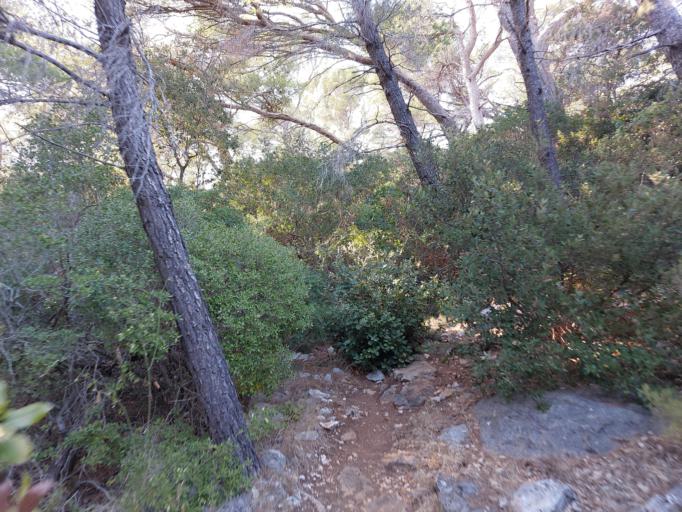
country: HR
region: Dubrovacko-Neretvanska
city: Smokvica
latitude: 42.7653
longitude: 16.8045
